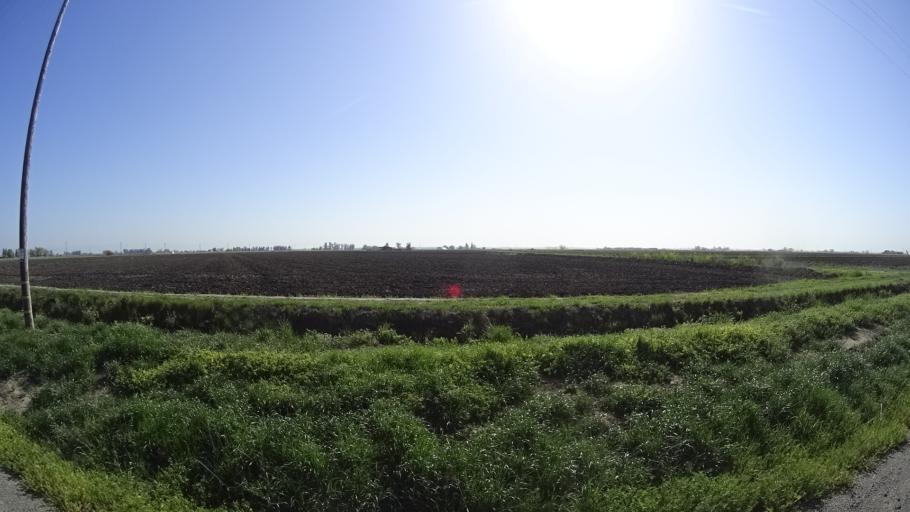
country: US
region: California
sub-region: Glenn County
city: Willows
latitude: 39.5810
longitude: -122.0841
